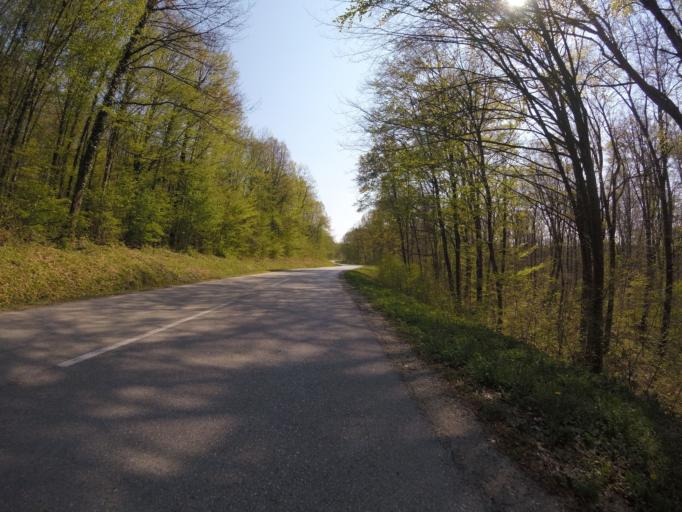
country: HR
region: Zagrebacka
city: Lukavec
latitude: 45.6349
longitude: 15.9624
